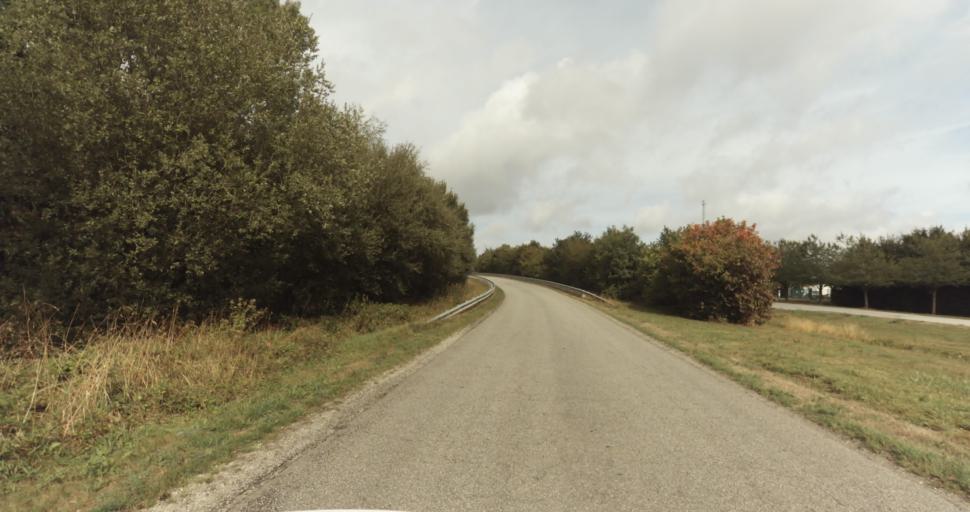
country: FR
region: Lower Normandy
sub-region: Departement de l'Orne
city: Gace
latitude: 48.8460
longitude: 0.3726
